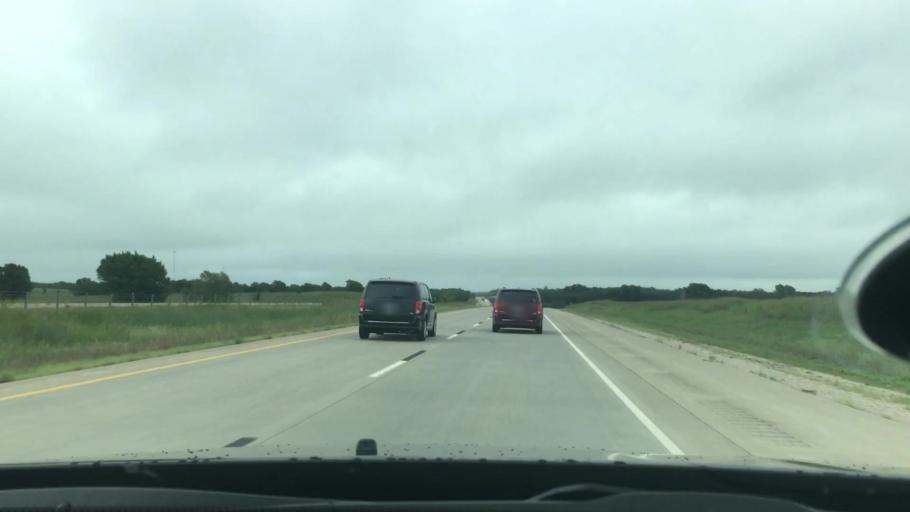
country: US
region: Oklahoma
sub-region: Okfuskee County
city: Boley
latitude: 35.3851
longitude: -96.4906
